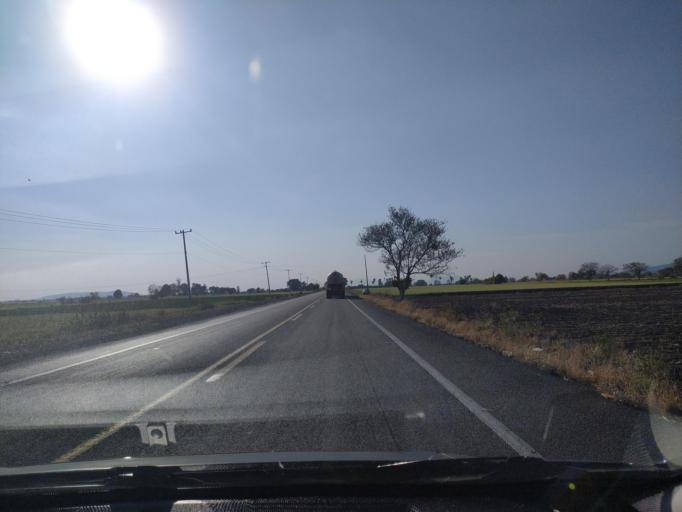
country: MX
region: Michoacan
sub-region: Yurecuaro
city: Yurecuaro
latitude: 20.3278
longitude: -102.2546
